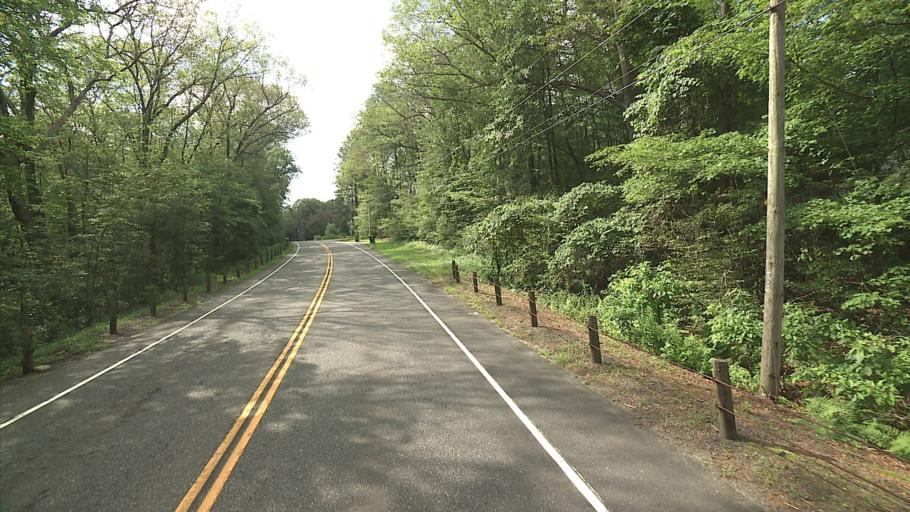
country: US
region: Connecticut
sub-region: Middlesex County
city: Chester Center
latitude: 41.3795
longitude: -72.5086
